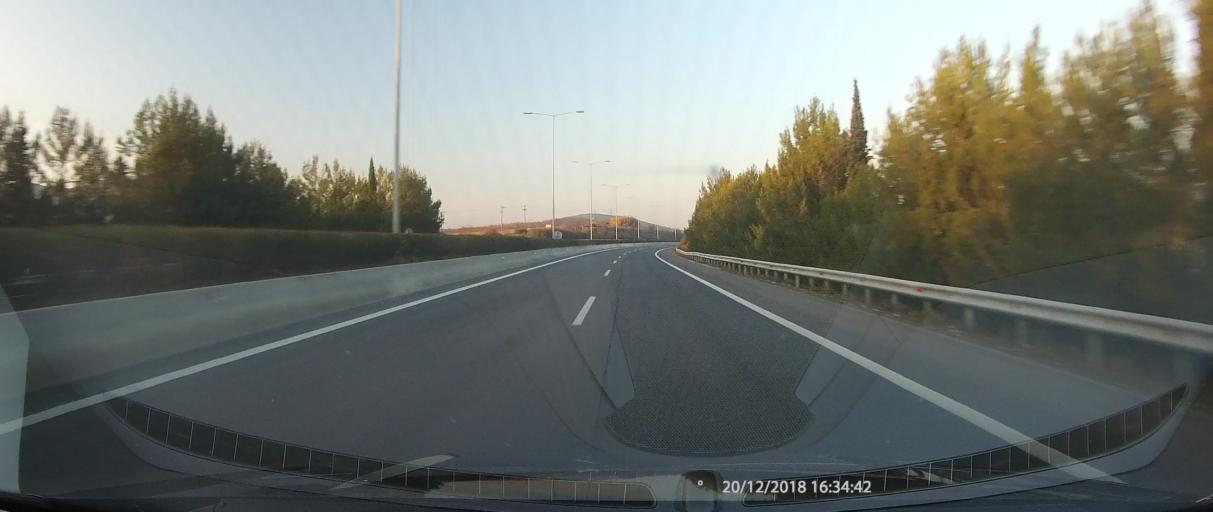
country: GR
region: Thessaly
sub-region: Nomos Magnisias
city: Nea Anchialos
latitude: 39.2881
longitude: 22.7443
